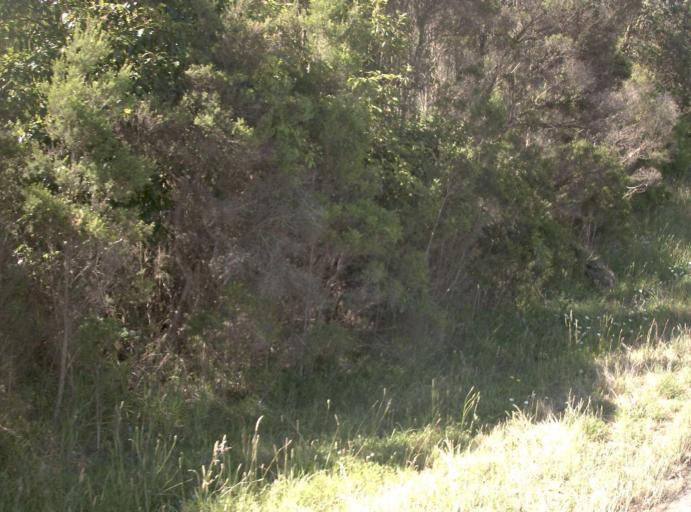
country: AU
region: Victoria
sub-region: Latrobe
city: Morwell
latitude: -38.6603
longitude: 146.4527
